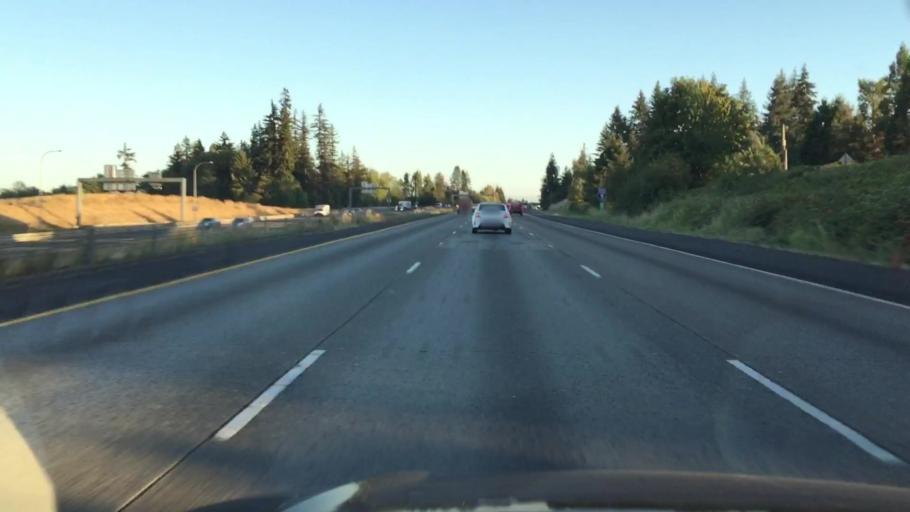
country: US
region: Washington
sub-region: Clark County
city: Mount Vista
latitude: 45.7721
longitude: -122.6698
